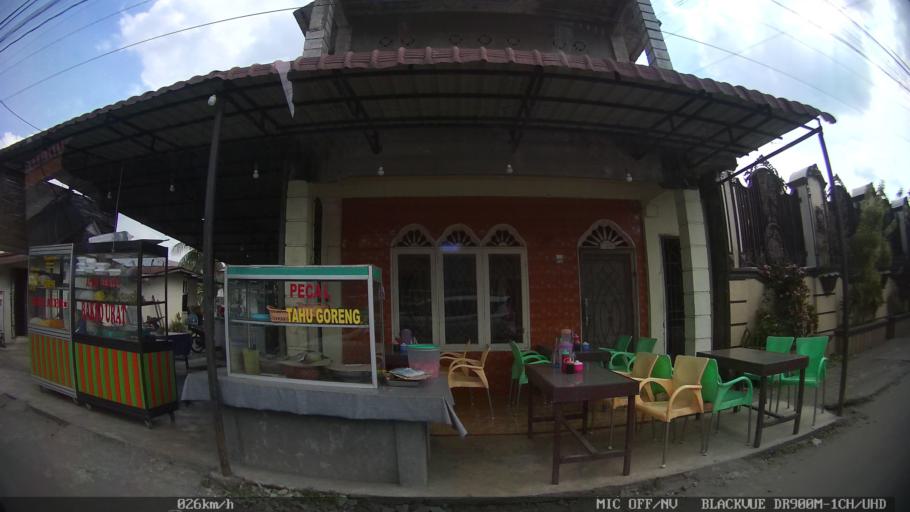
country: ID
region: North Sumatra
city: Binjai
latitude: 3.6131
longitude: 98.5063
